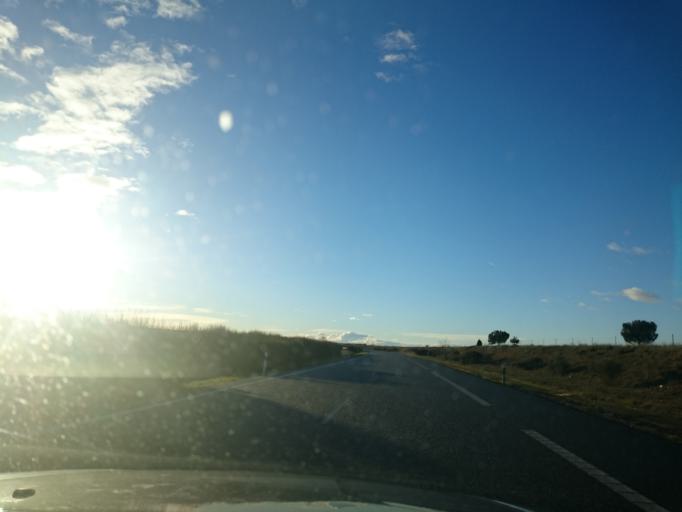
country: ES
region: Castille and Leon
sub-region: Provincia de Leon
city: Vega de Infanzones
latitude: 42.4742
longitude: -5.5501
